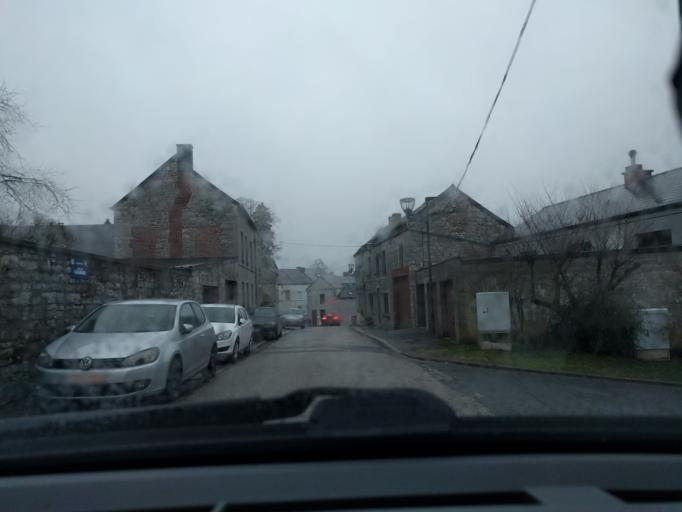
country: BE
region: Wallonia
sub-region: Province de Namur
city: Couvin
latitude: 50.0506
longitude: 4.5005
